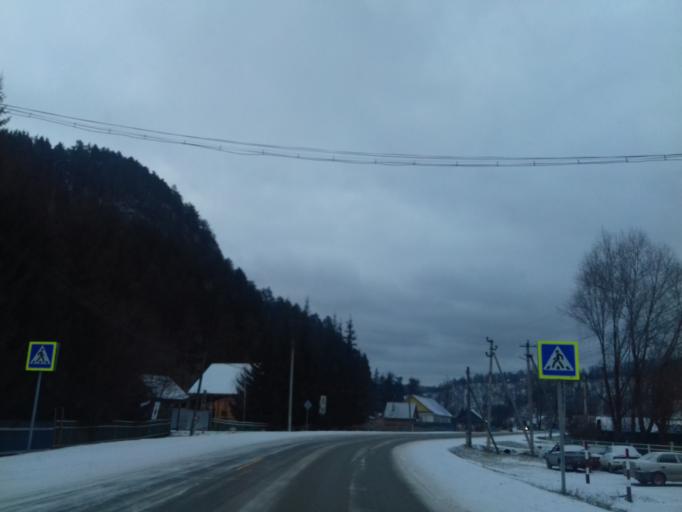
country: RU
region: Bashkortostan
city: Starosubkhangulovo
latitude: 53.1213
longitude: 57.4221
